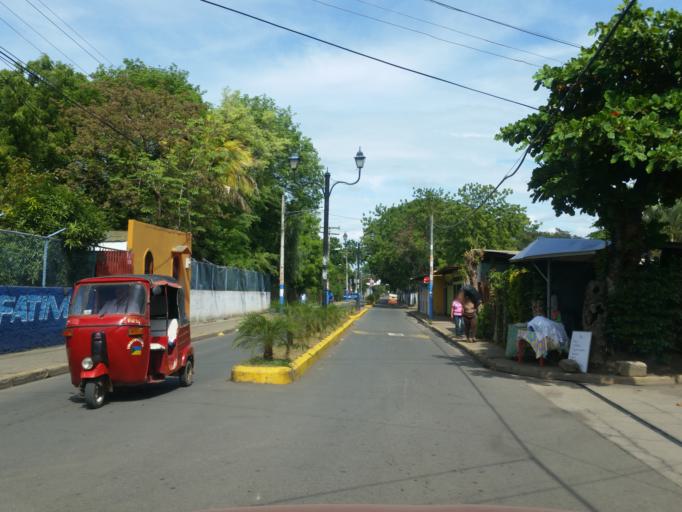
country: NI
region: Masaya
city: Nindiri
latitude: 12.0016
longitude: -86.1183
